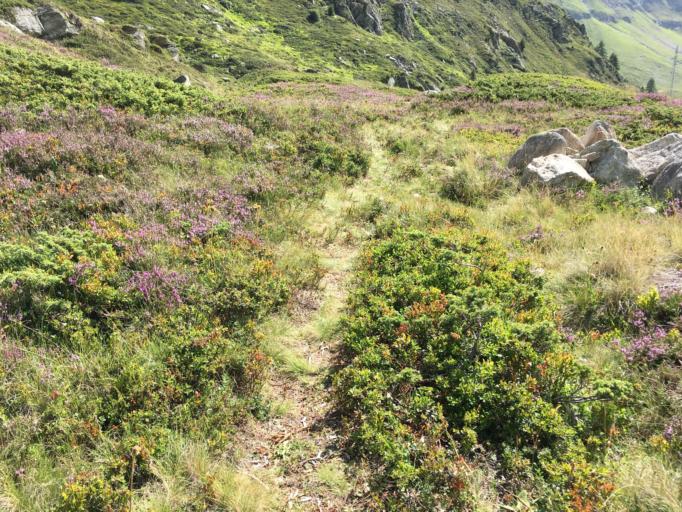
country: CH
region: Grisons
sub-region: Maloja District
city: Silvaplana
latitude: 46.4645
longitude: 9.6899
